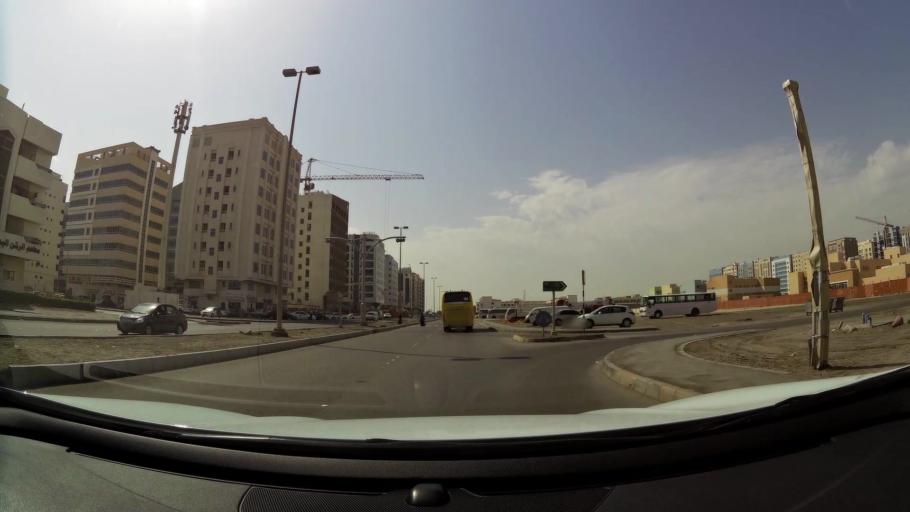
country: AE
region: Abu Dhabi
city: Abu Dhabi
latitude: 24.3381
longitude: 54.5349
